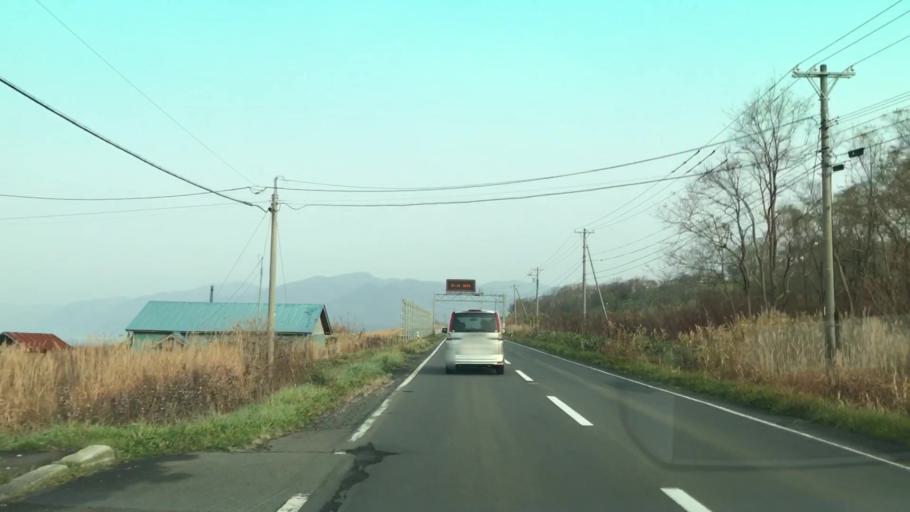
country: JP
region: Hokkaido
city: Ishikari
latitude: 43.3764
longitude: 141.4280
